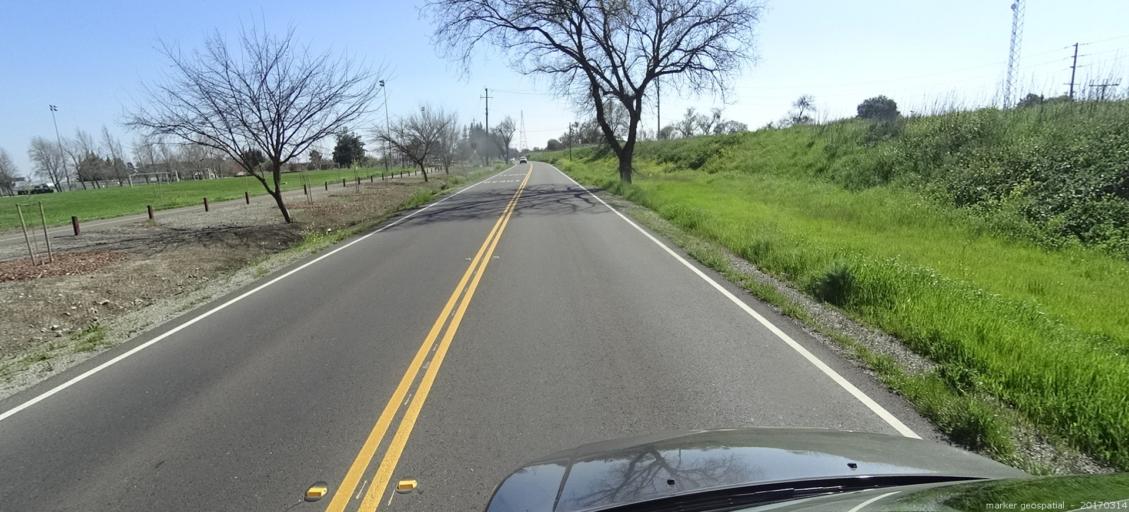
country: US
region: California
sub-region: Sacramento County
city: Parkway
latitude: 38.4734
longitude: -121.5041
